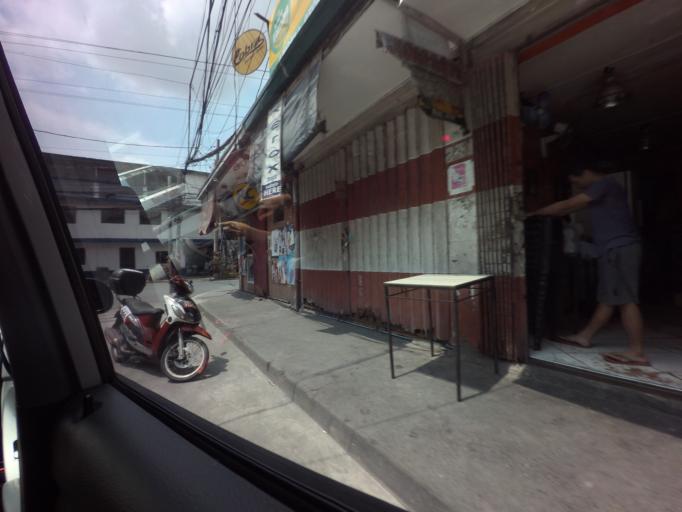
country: PH
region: Metro Manila
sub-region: City of Manila
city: Quiapo
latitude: 14.5925
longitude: 121.0044
